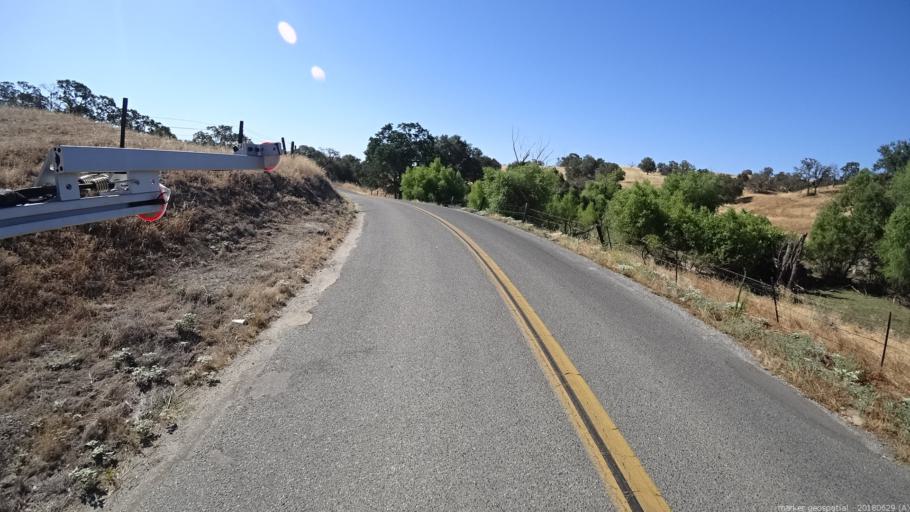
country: US
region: California
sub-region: Madera County
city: Yosemite Lakes
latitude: 37.0846
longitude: -119.7981
